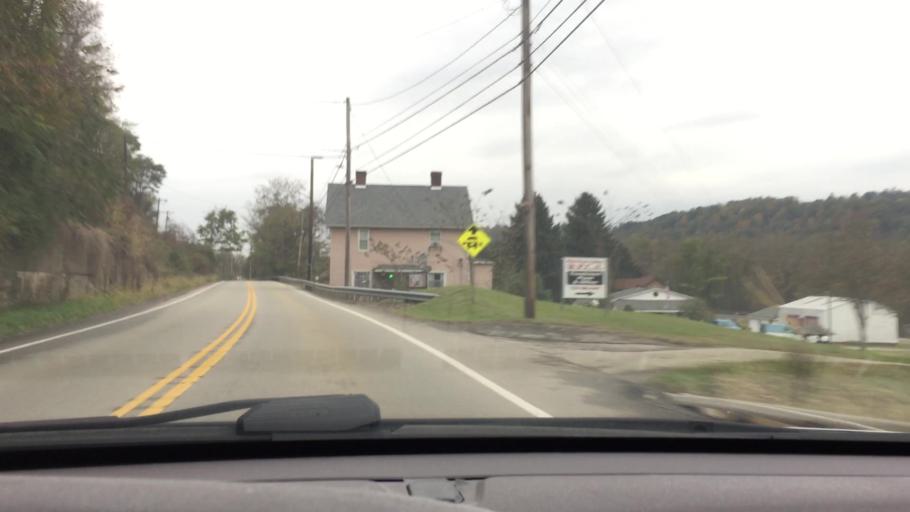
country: US
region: Pennsylvania
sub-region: Fayette County
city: Fairhope
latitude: 40.1084
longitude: -79.8498
